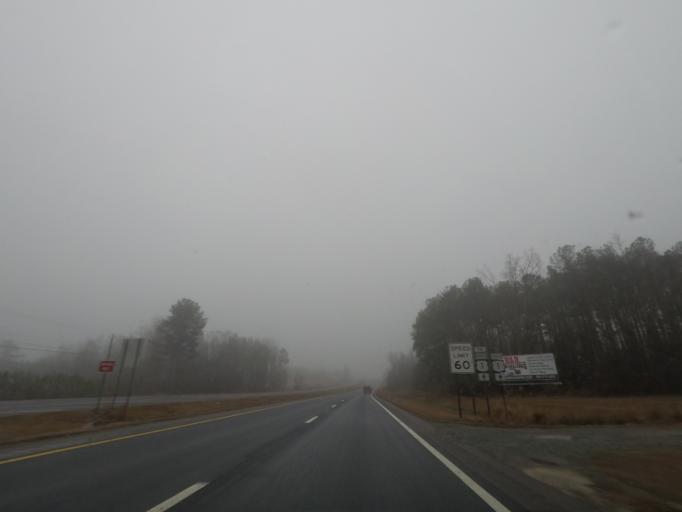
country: US
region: North Carolina
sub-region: Lee County
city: Sanford
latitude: 35.3892
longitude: -79.2312
